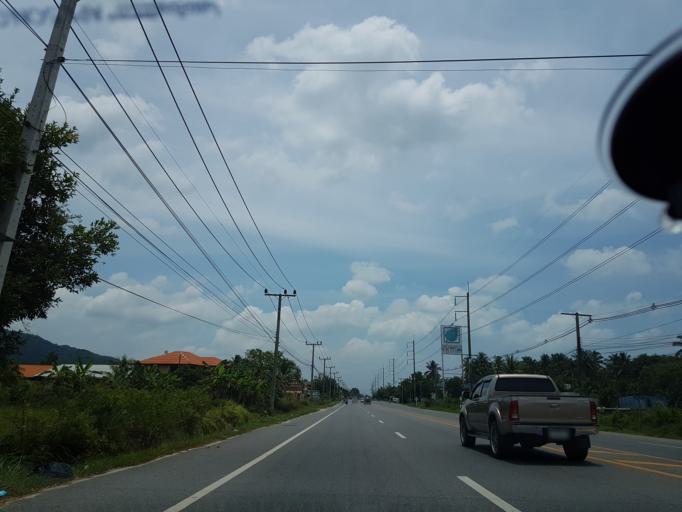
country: TH
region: Songkhla
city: Songkhla
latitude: 7.0981
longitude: 100.6339
